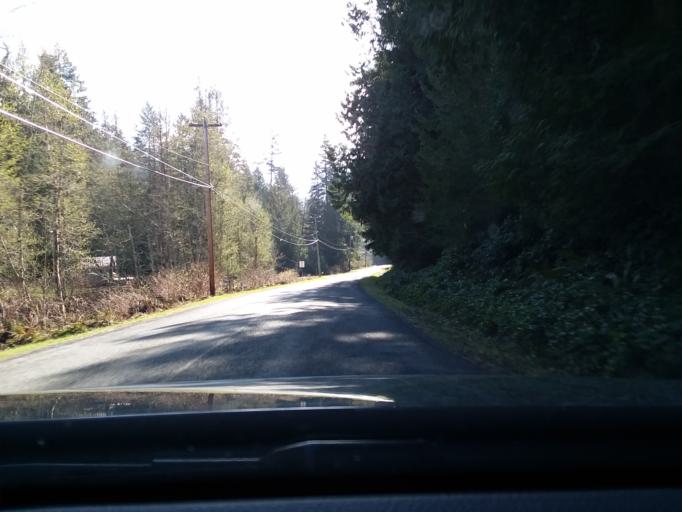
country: CA
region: British Columbia
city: North Cowichan
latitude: 48.9290
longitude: -123.4619
